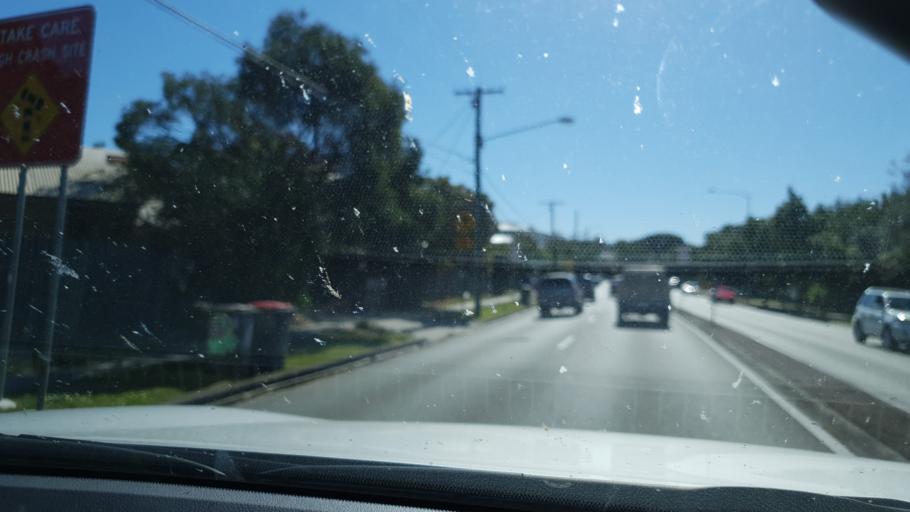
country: AU
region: Queensland
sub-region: Brisbane
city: Everton Park
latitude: -27.4040
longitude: 152.9882
